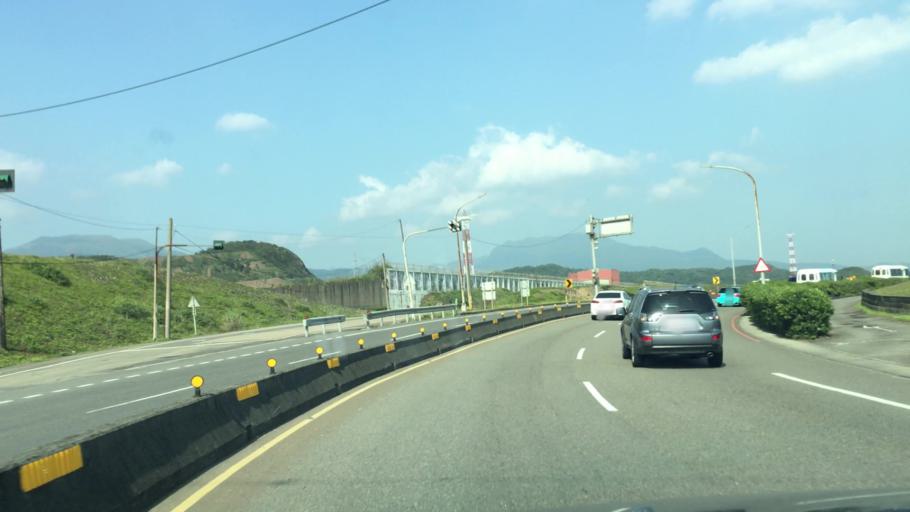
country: TW
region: Taiwan
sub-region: Keelung
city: Keelung
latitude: 25.2011
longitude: 121.6720
